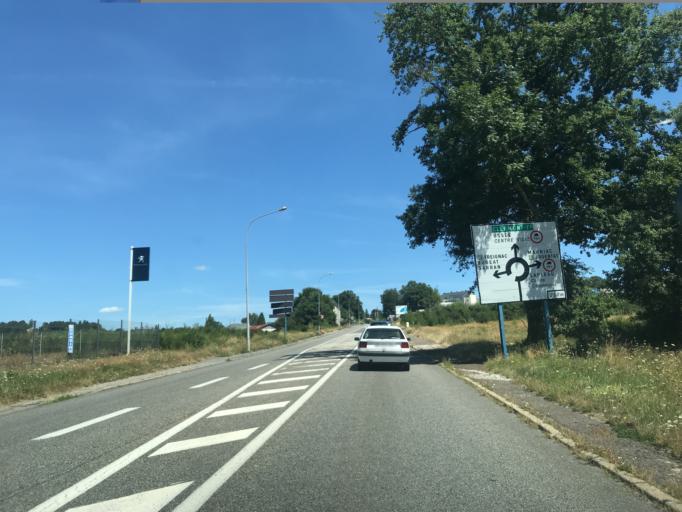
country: FR
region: Limousin
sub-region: Departement de la Correze
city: Egletons
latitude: 45.3989
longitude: 2.0365
